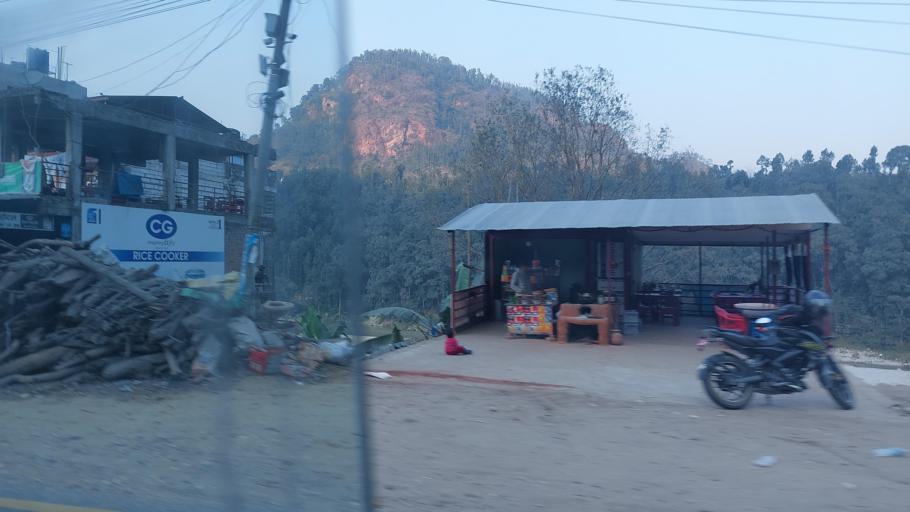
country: NP
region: Central Region
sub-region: Narayani Zone
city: Bharatpur
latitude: 27.8046
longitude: 84.8367
